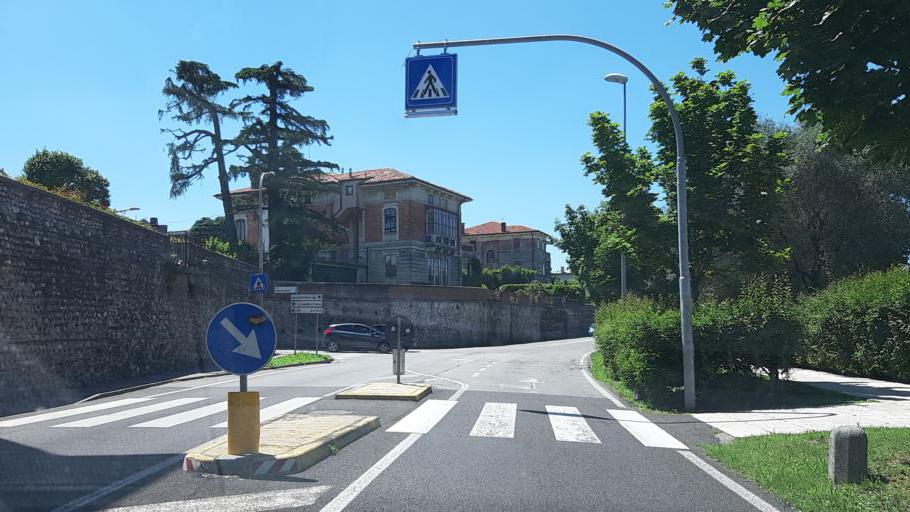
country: IT
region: Veneto
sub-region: Provincia di Vicenza
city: Bassano del Grappa
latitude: 45.7715
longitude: 11.7401
